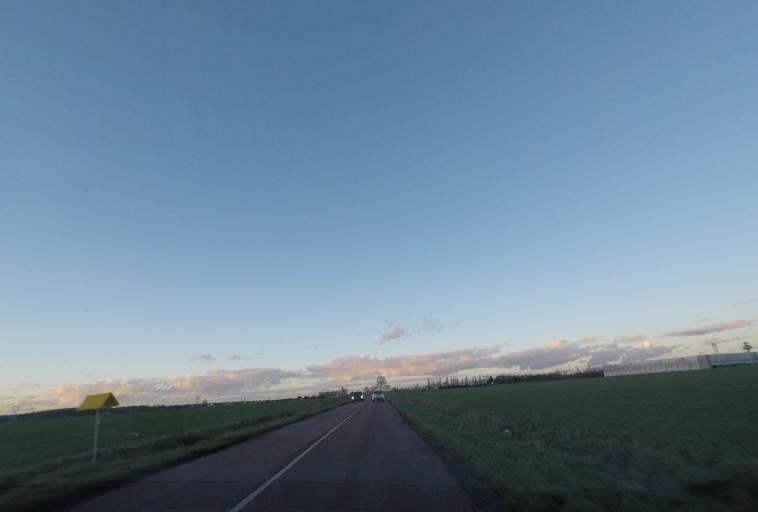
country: FR
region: Ile-de-France
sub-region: Departement de l'Essonne
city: Villabe
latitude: 48.5853
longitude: 2.4323
